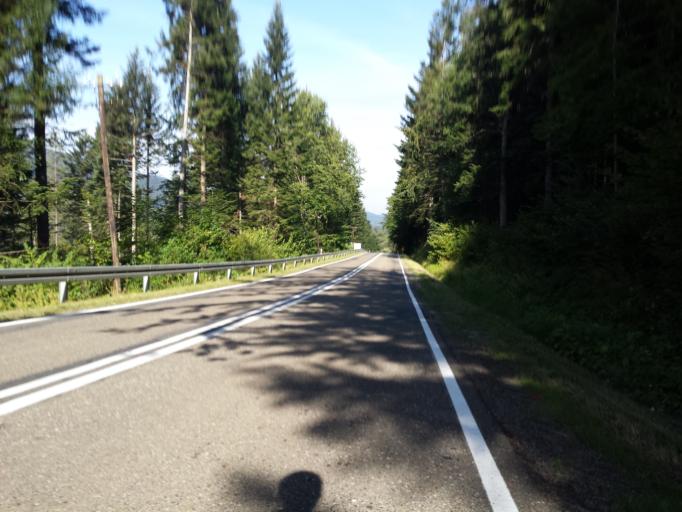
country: PL
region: Subcarpathian Voivodeship
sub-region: Powiat leski
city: Cisna
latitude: 49.2425
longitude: 22.2959
